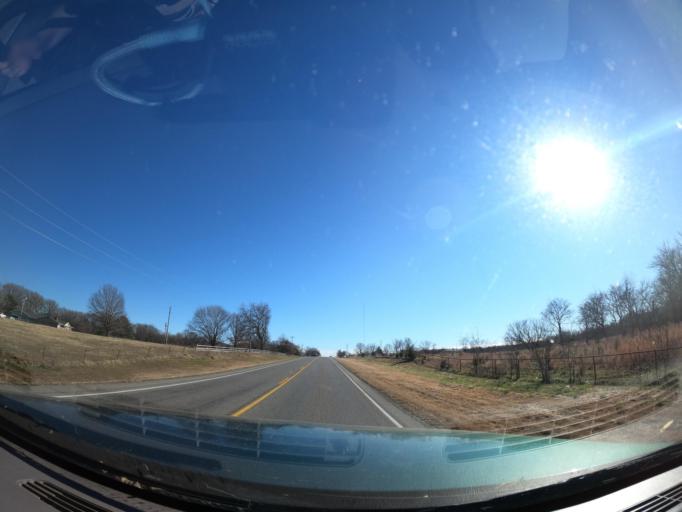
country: US
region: Oklahoma
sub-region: Muskogee County
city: Haskell
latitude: 35.7709
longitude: -95.6541
